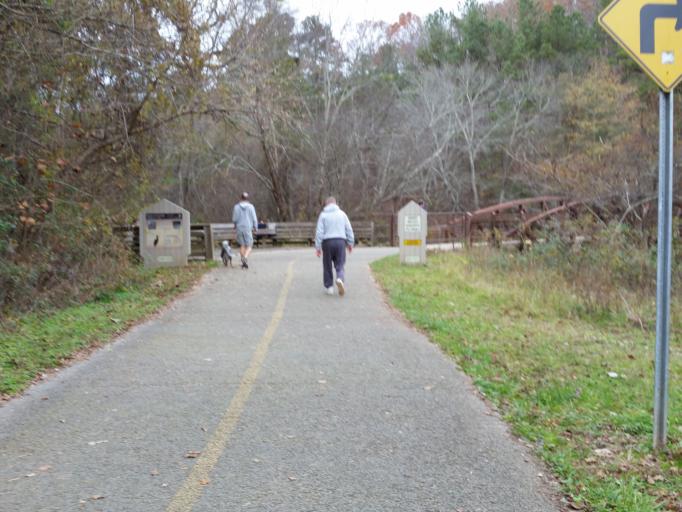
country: US
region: Georgia
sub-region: Cobb County
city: Vinings
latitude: 33.8766
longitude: -84.4482
